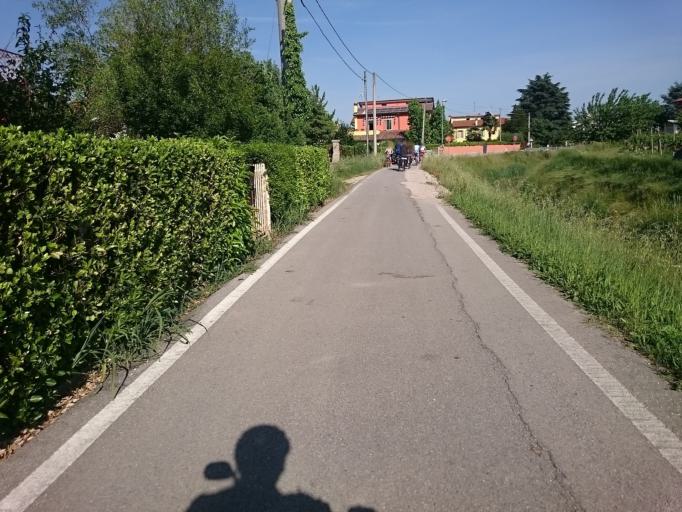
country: IT
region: Veneto
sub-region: Provincia di Padova
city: Torreglia
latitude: 45.3410
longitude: 11.7572
